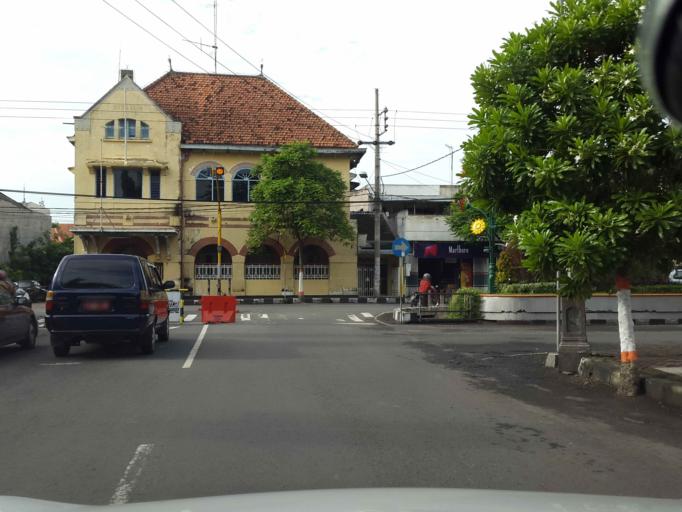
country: ID
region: East Java
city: Mojokerto
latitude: -7.4634
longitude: 112.4326
